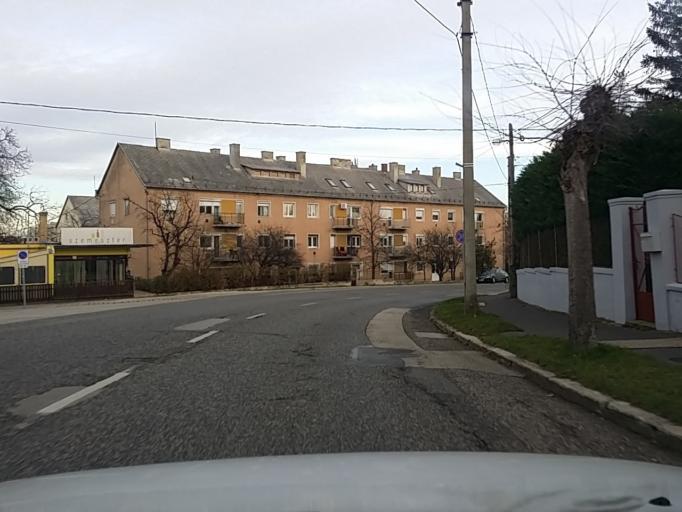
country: HU
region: Veszprem
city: Veszprem
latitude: 47.0892
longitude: 17.9045
